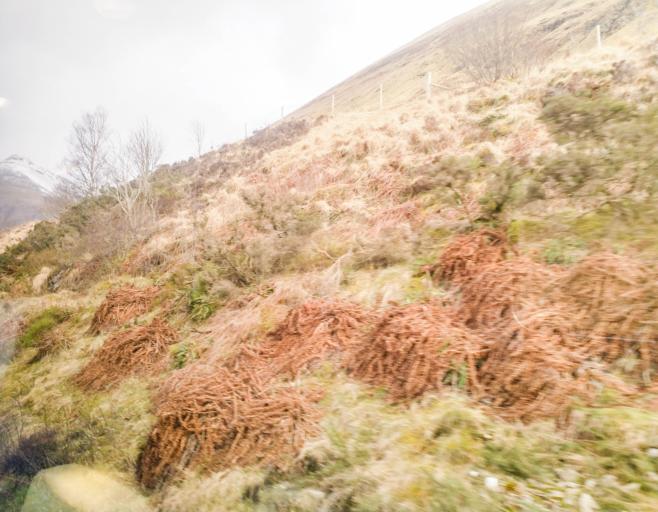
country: GB
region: Scotland
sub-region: Argyll and Bute
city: Garelochhead
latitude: 56.4617
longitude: -4.7147
